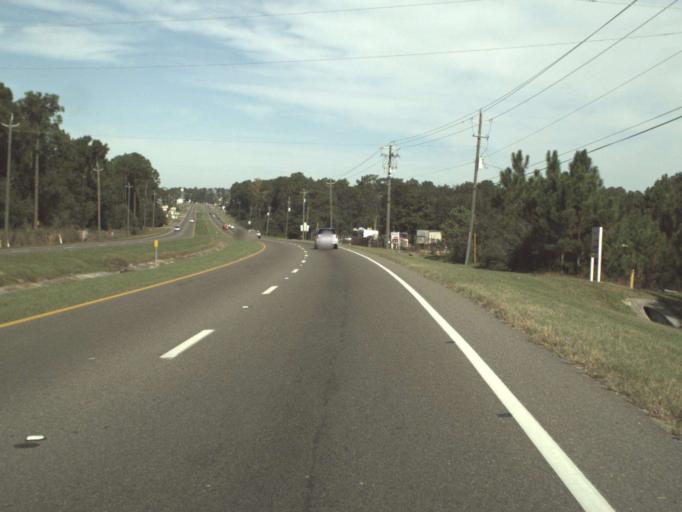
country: US
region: Florida
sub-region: Escambia County
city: Ensley
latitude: 30.5055
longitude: -87.3060
